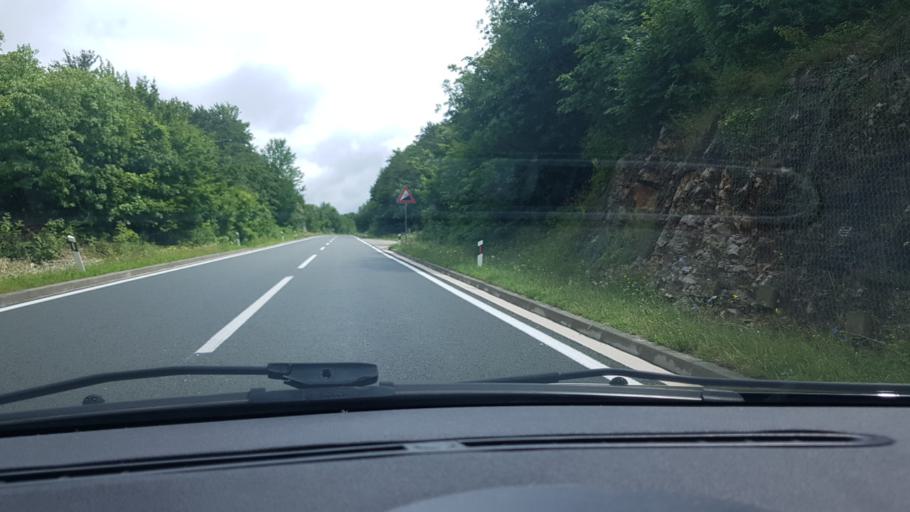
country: HR
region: Licko-Senjska
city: Jezerce
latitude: 44.8836
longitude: 15.6927
